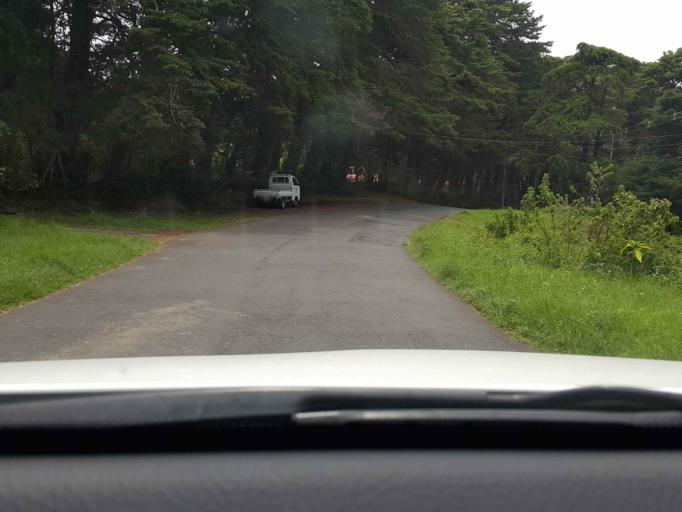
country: CR
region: Heredia
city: San Josecito
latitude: 10.0529
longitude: -84.0887
